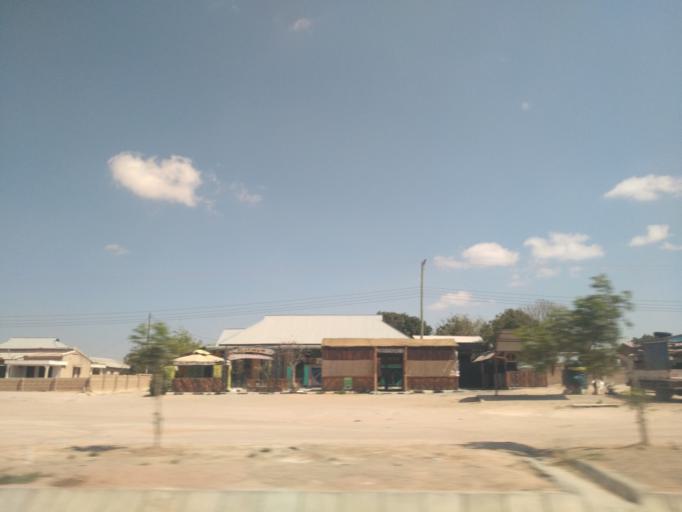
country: TZ
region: Dodoma
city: Dodoma
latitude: -6.1513
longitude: 35.7271
